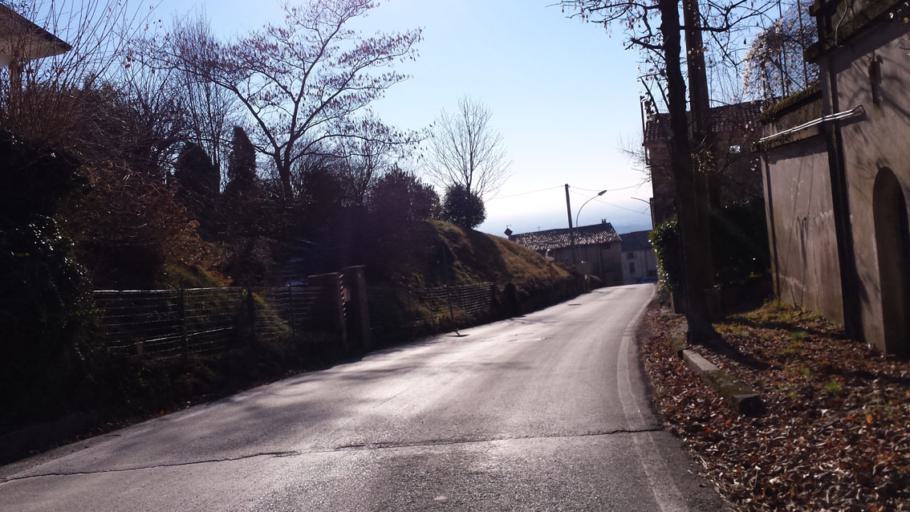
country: IT
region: Veneto
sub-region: Provincia di Treviso
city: Crespano del Grappa
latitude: 45.8470
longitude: 11.8446
